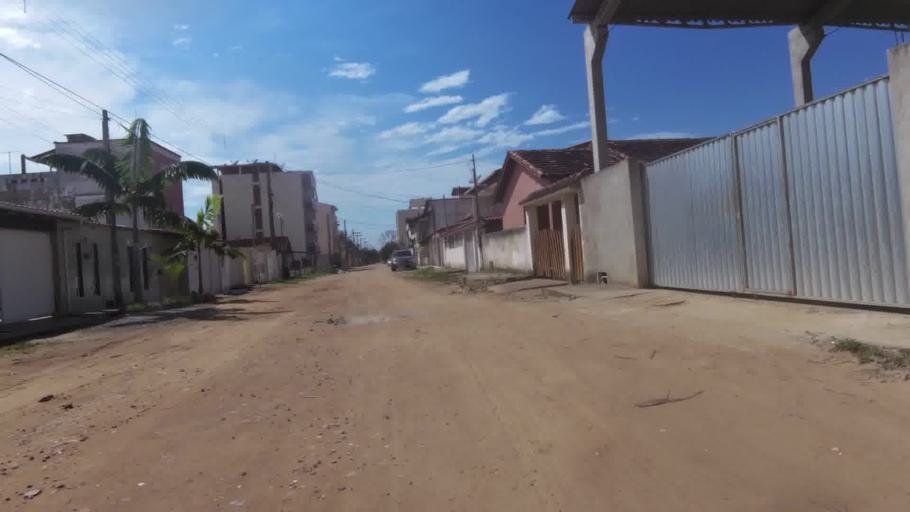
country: BR
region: Espirito Santo
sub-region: Piuma
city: Piuma
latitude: -20.8434
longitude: -40.7438
